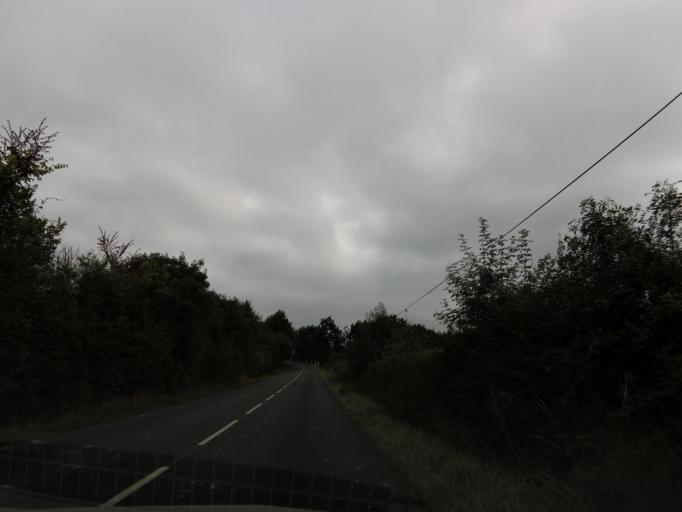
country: FR
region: Pays de la Loire
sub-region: Departement de la Vendee
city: Moutiers-les-Mauxfaits
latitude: 46.4772
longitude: -1.4453
